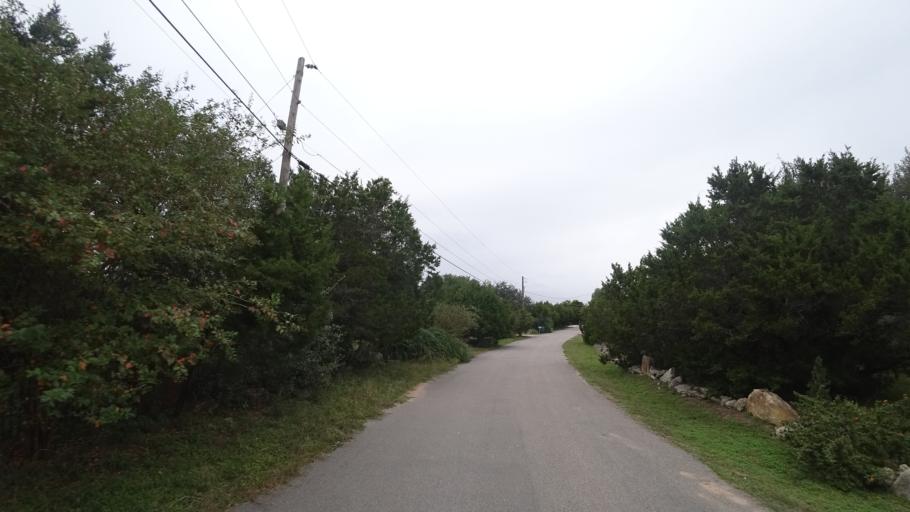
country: US
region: Texas
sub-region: Travis County
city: Hudson Bend
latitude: 30.3725
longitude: -97.9257
